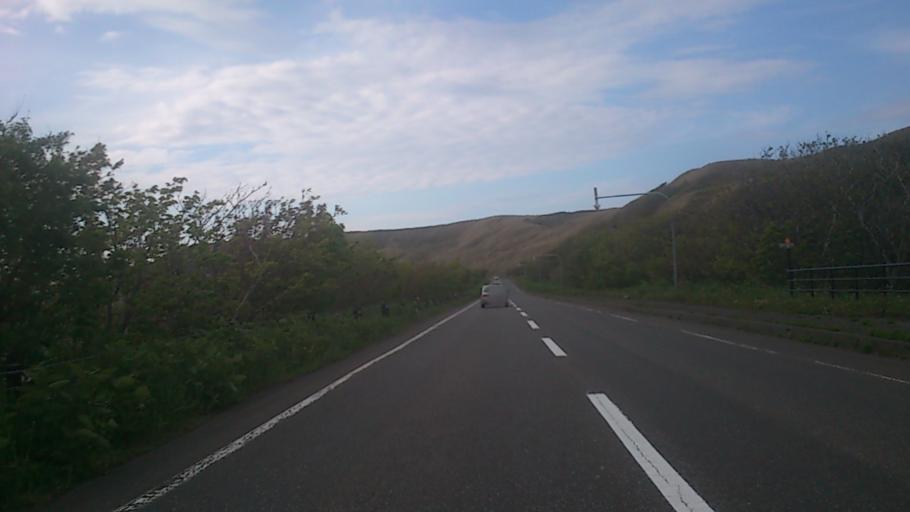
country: JP
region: Hokkaido
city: Wakkanai
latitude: 45.3635
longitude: 141.6619
